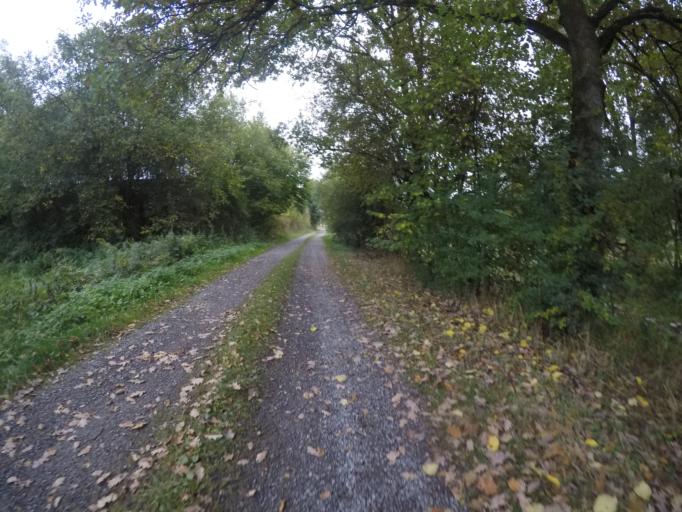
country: BE
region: Wallonia
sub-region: Province du Luxembourg
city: Fauvillers
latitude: 49.9016
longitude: 5.6870
